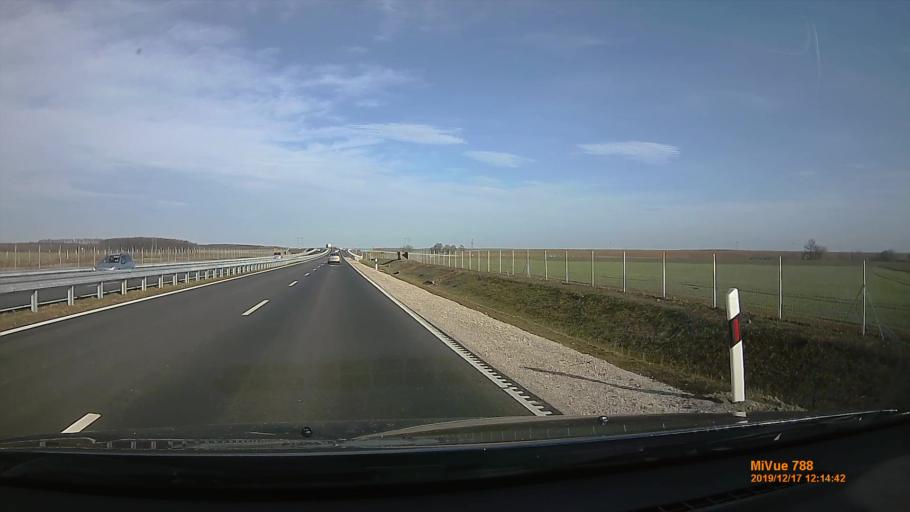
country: HU
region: Somogy
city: Kaposvar
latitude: 46.4672
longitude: 17.7975
